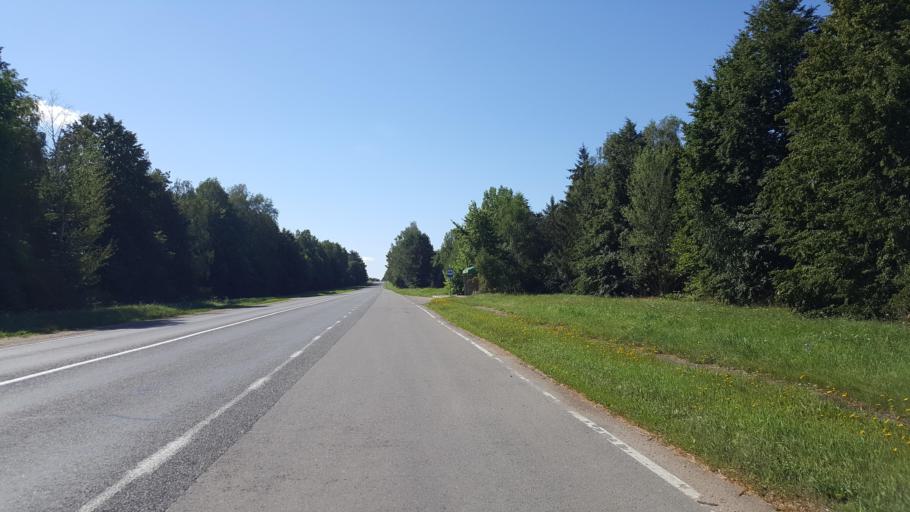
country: BY
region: Brest
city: Kamyanyets
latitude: 52.3547
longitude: 23.7758
